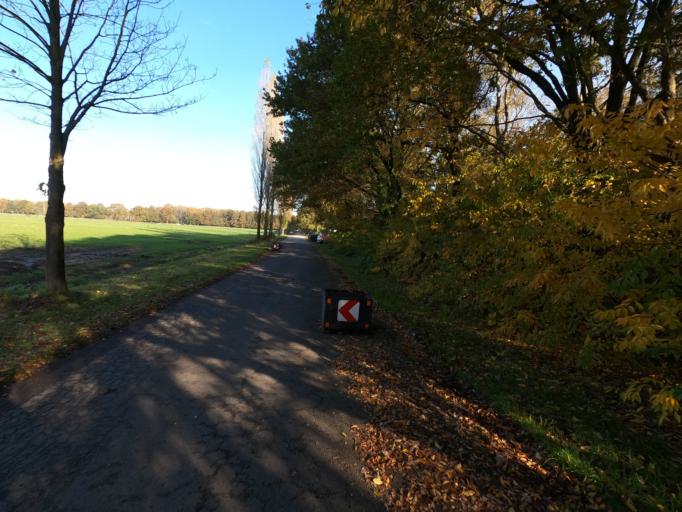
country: BE
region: Flanders
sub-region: Provincie Antwerpen
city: Wuustwezel
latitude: 51.3435
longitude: 4.5428
